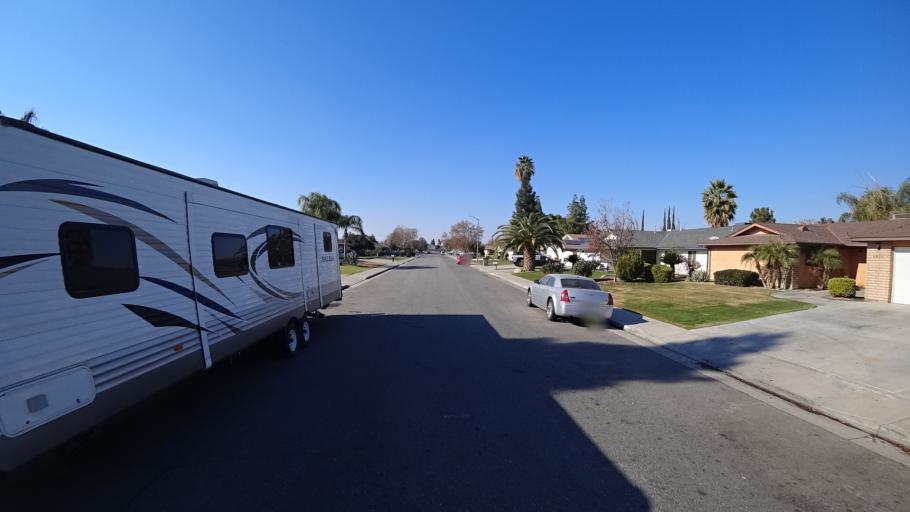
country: US
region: California
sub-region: Kern County
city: Greenfield
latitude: 35.2991
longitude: -119.0534
